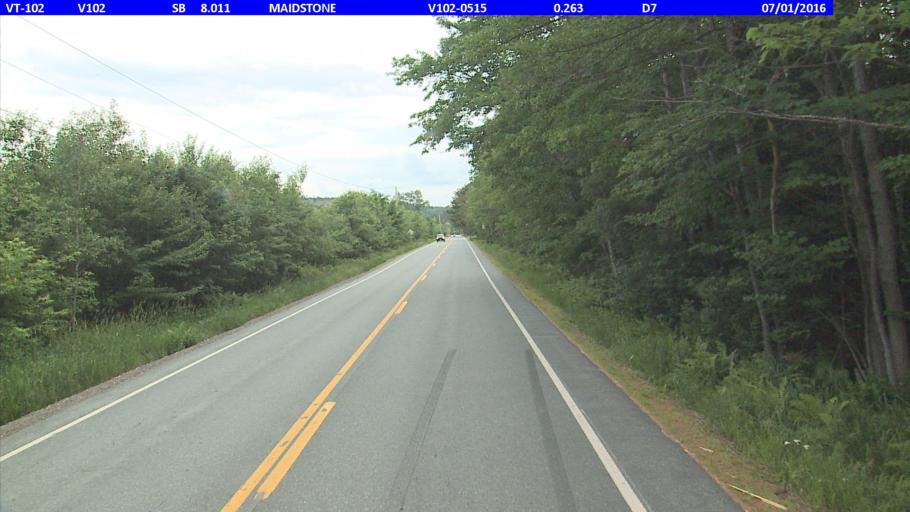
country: US
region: Vermont
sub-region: Essex County
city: Guildhall
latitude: 44.5744
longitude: -71.5549
